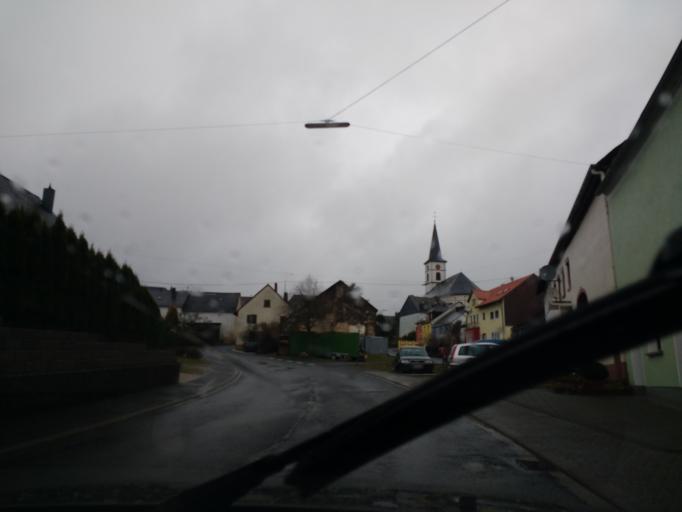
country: DE
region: Rheinland-Pfalz
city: Rascheid
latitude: 49.7265
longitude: 6.9183
